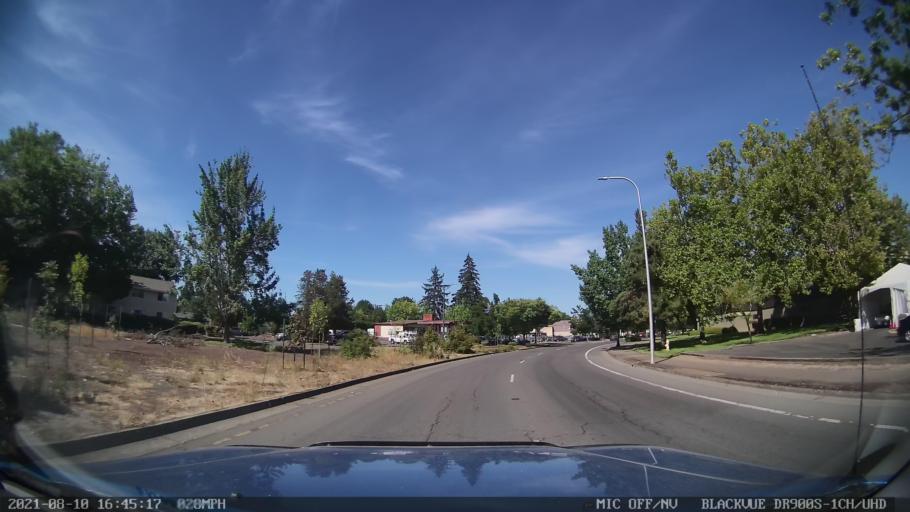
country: US
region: Oregon
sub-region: Marion County
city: Salem
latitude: 44.9556
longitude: -123.0208
